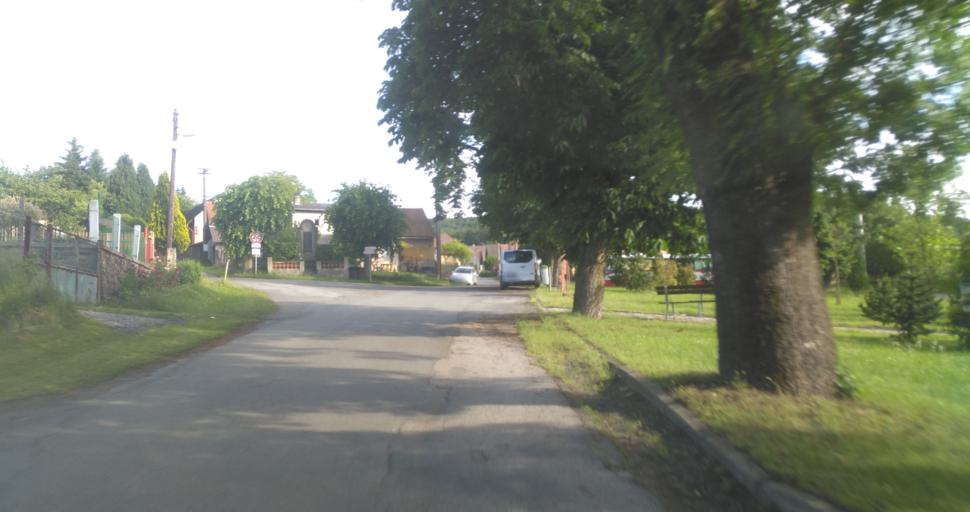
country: CZ
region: Central Bohemia
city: Roztoky
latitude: 50.0114
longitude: 13.8446
